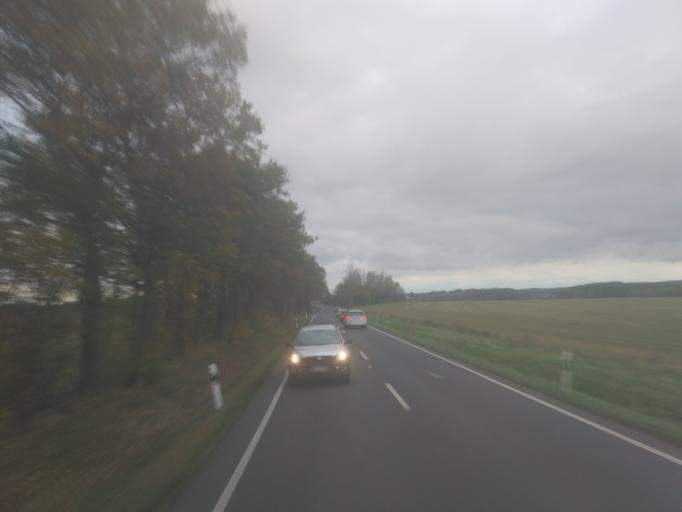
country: DE
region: Saxony
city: Grossenhain
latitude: 51.3312
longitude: 13.5436
